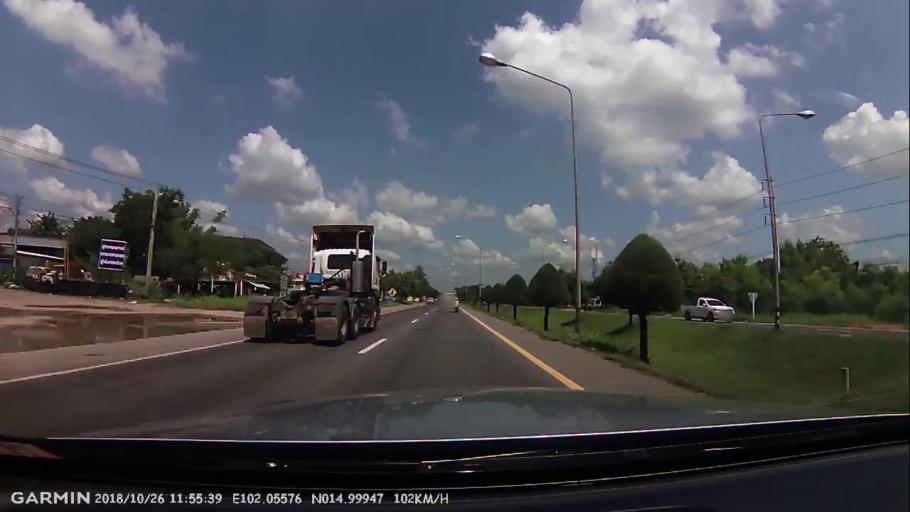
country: TH
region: Nakhon Ratchasima
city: Nakhon Ratchasima
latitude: 14.9996
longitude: 102.0558
